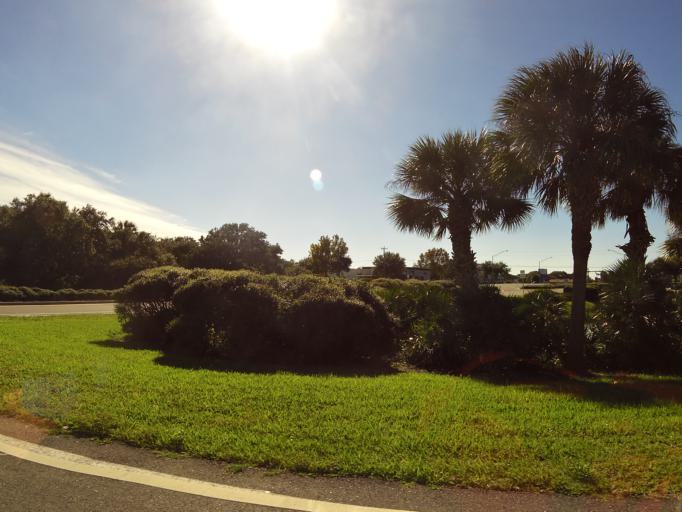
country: US
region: Florida
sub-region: Saint Johns County
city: Saint Augustine Beach
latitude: 29.8611
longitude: -81.2786
